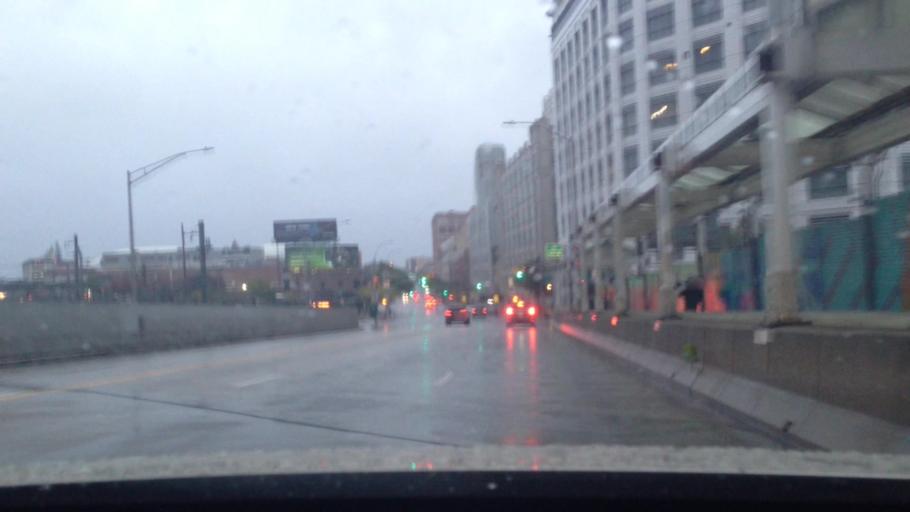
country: US
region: New York
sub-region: Queens County
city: Long Island City
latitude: 40.7455
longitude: -73.9389
